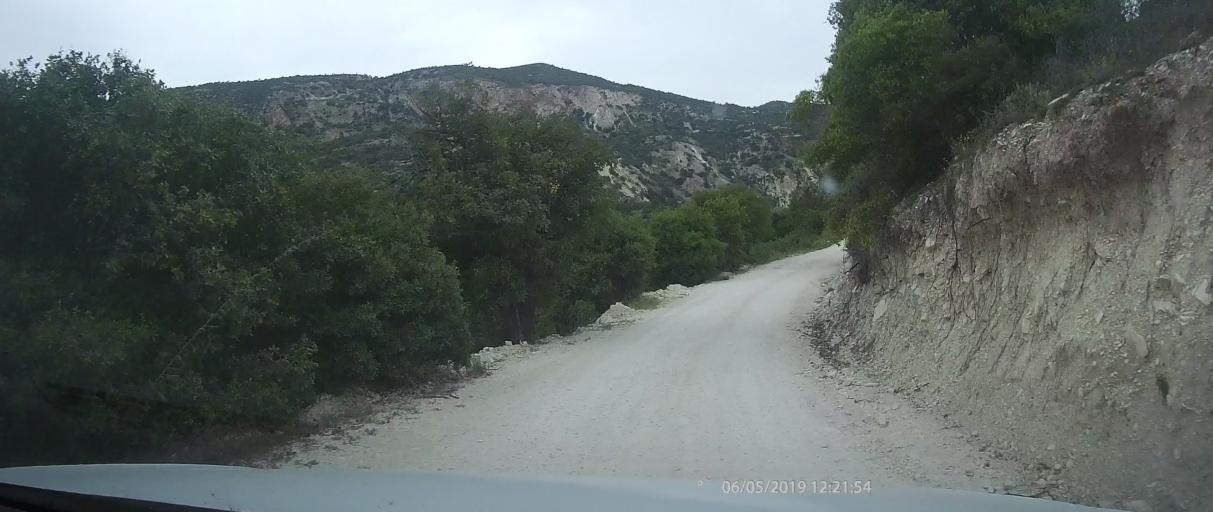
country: CY
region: Pafos
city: Tala
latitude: 34.8658
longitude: 32.4328
